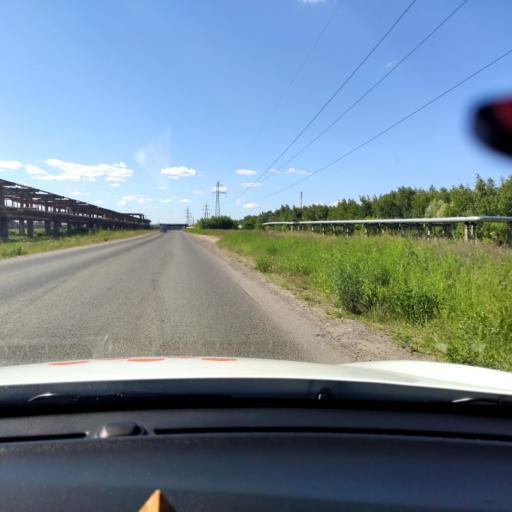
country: RU
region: Tatarstan
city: Staroye Arakchino
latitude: 55.8757
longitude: 48.9754
